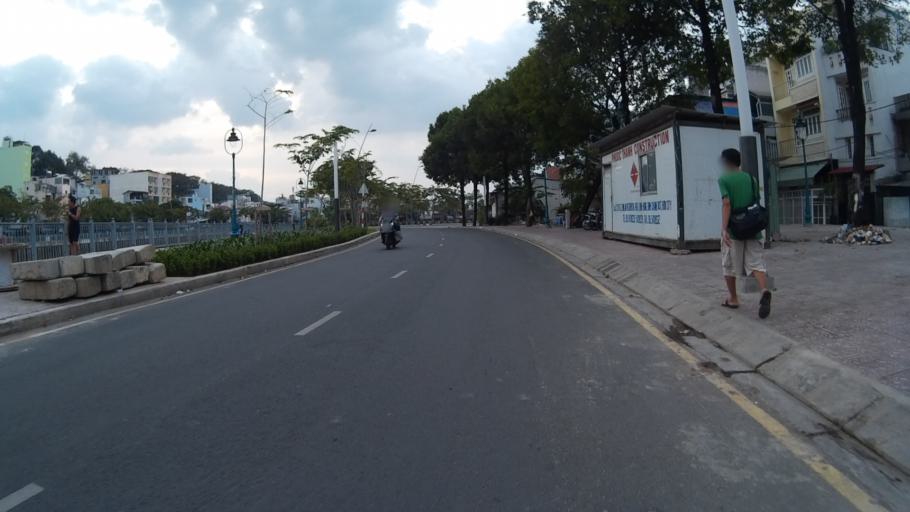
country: VN
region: Ho Chi Minh City
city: Quan Binh Thanh
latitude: 10.7939
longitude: 106.6960
